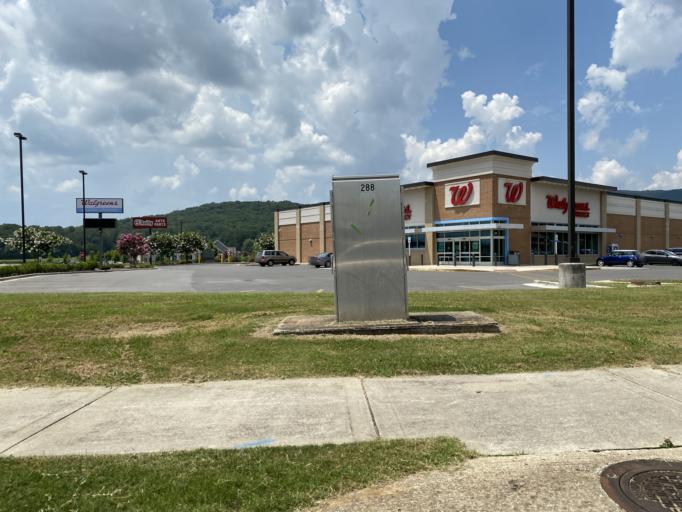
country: US
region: Alabama
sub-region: Madison County
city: Owens Cross Roads
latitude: 34.6598
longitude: -86.4887
